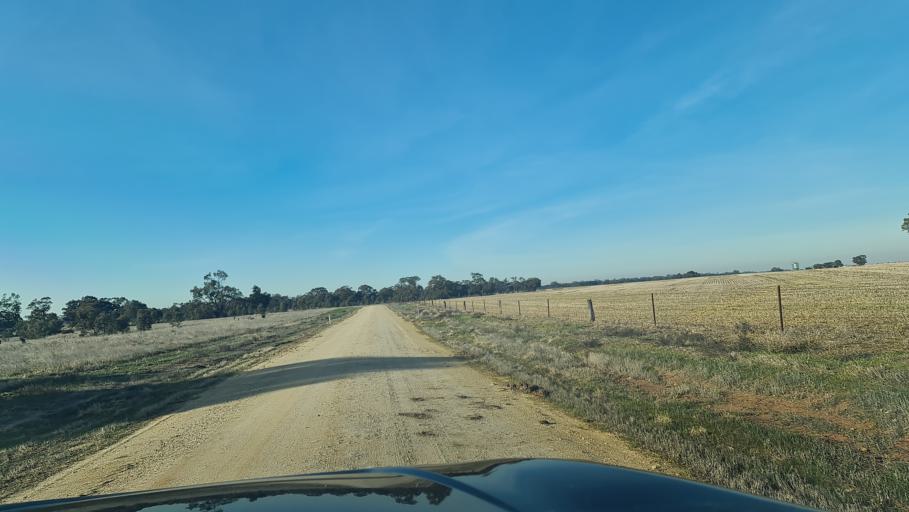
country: AU
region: Victoria
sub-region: Horsham
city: Horsham
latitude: -36.3545
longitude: 142.3947
